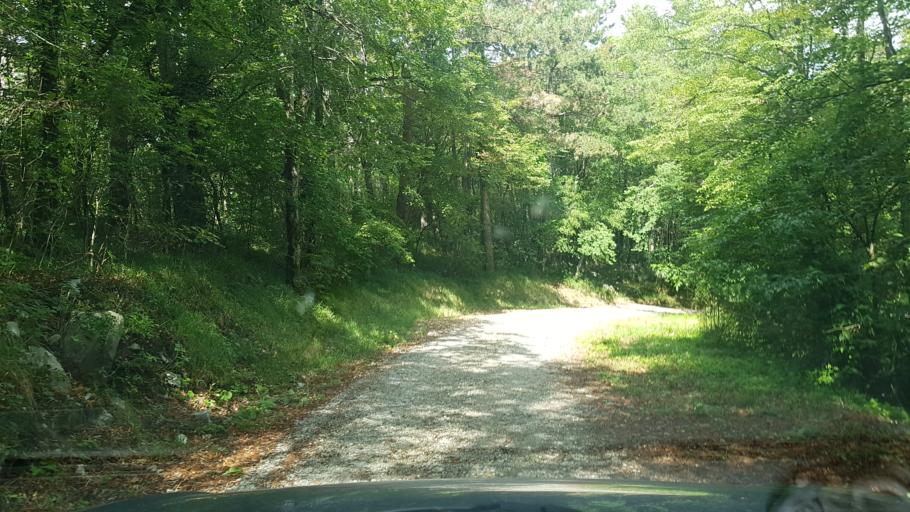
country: SI
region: Nova Gorica
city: Solkan
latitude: 46.0029
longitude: 13.6519
